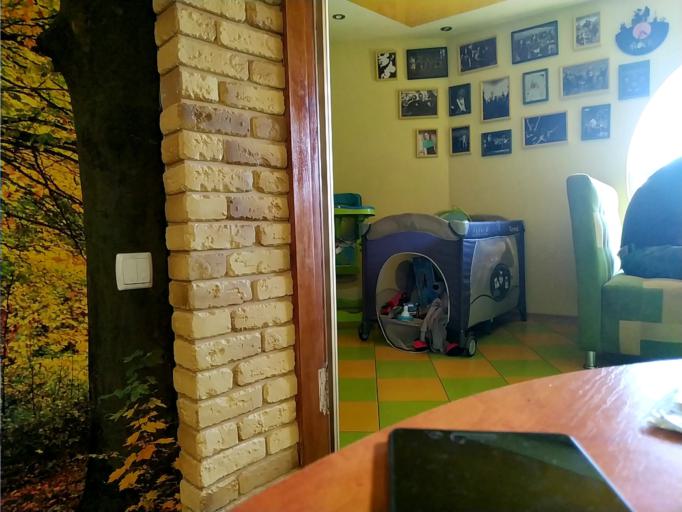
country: RU
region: Rjazan
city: Putyatino
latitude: 53.9668
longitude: 41.2917
